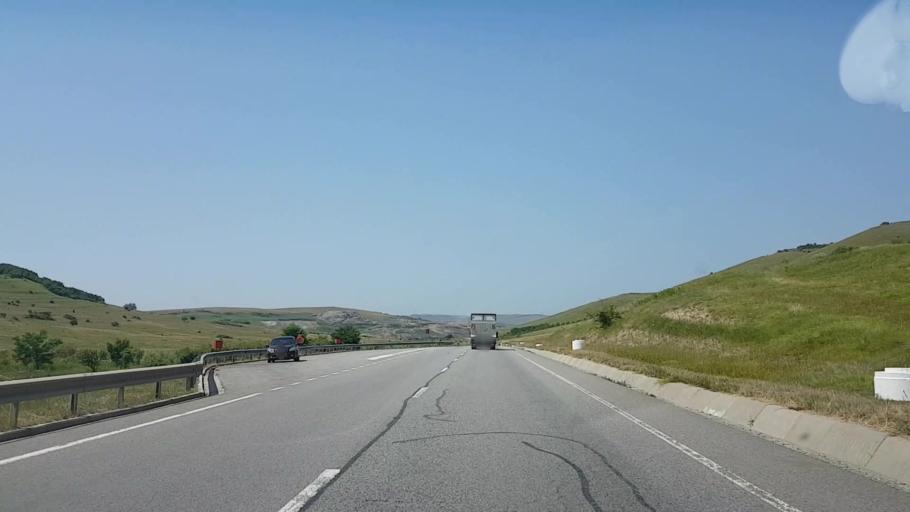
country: RO
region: Cluj
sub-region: Comuna Apahida
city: Dezmir
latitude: 46.7507
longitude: 23.7048
